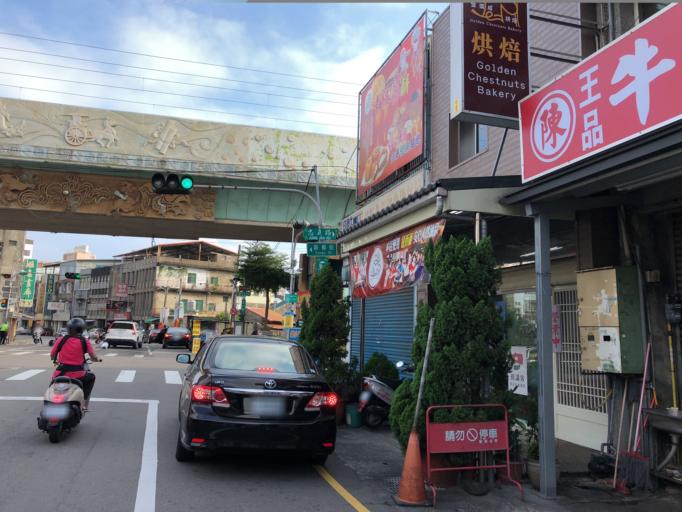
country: TW
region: Taiwan
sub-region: Miaoli
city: Miaoli
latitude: 24.5585
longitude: 120.8176
